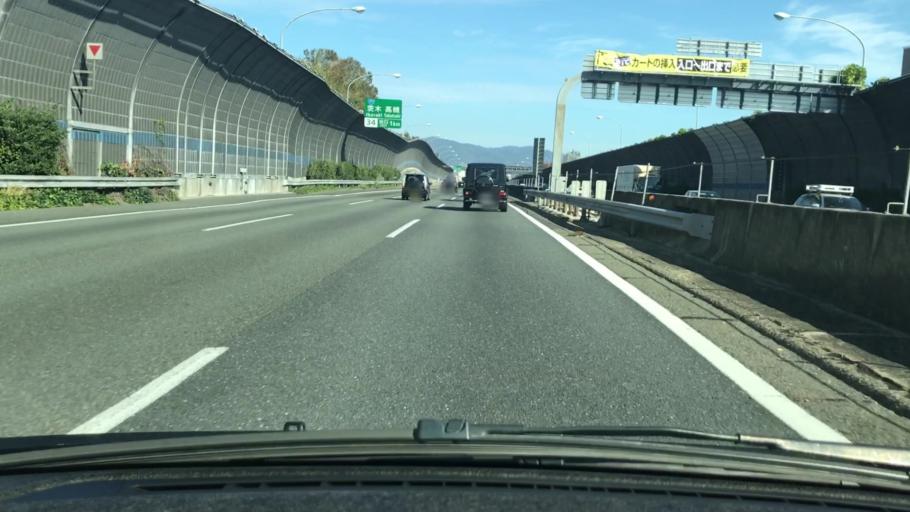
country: JP
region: Osaka
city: Ibaraki
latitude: 34.8214
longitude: 135.5529
